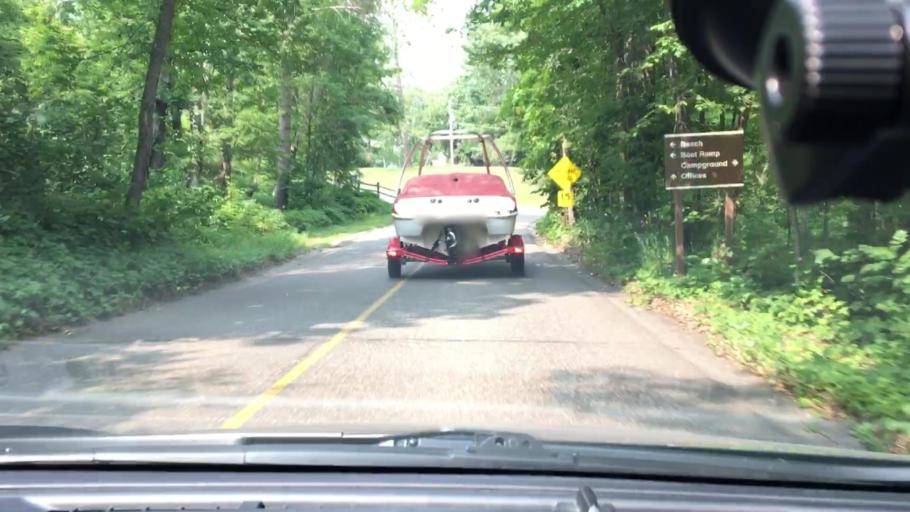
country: US
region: Minnesota
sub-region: Cass County
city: East Gull Lake
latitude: 46.4103
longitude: -94.3541
